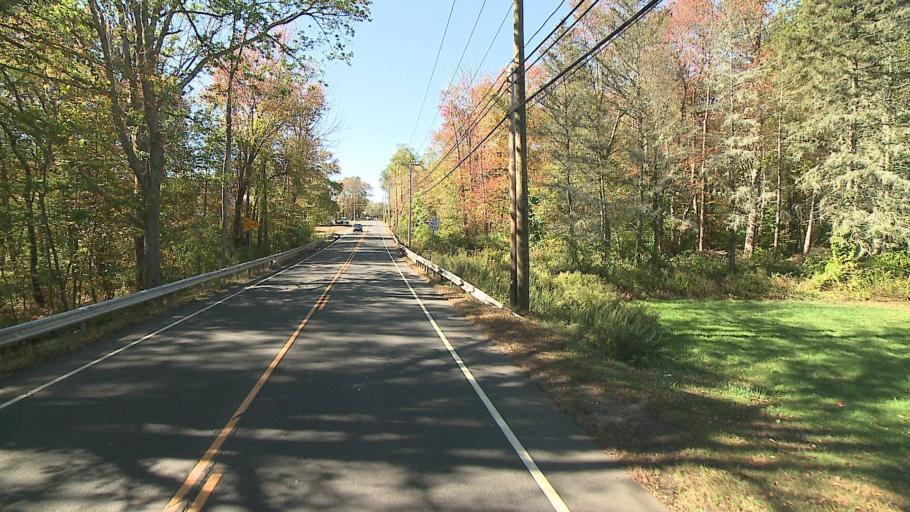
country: US
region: Connecticut
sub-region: Middlesex County
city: East Hampton
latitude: 41.5691
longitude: -72.5302
